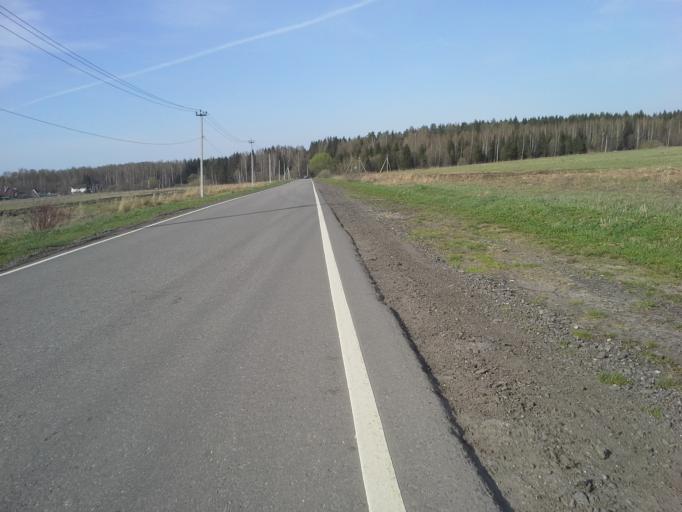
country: RU
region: Moskovskaya
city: Vatutinki
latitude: 55.4644
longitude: 37.3779
